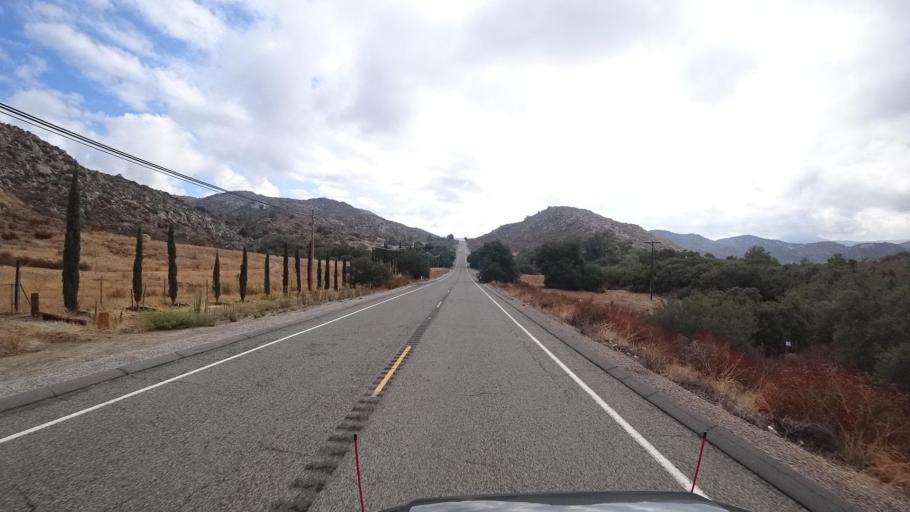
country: MX
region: Baja California
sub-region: Tecate
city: Hacienda Tecate
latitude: 32.5976
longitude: -116.5592
